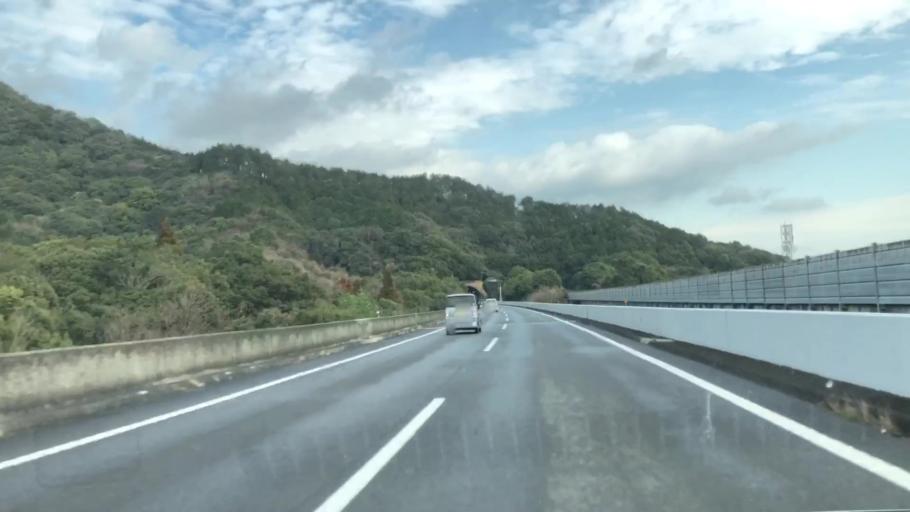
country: JP
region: Saga Prefecture
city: Kanzakimachi-kanzaki
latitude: 33.3393
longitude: 130.3513
